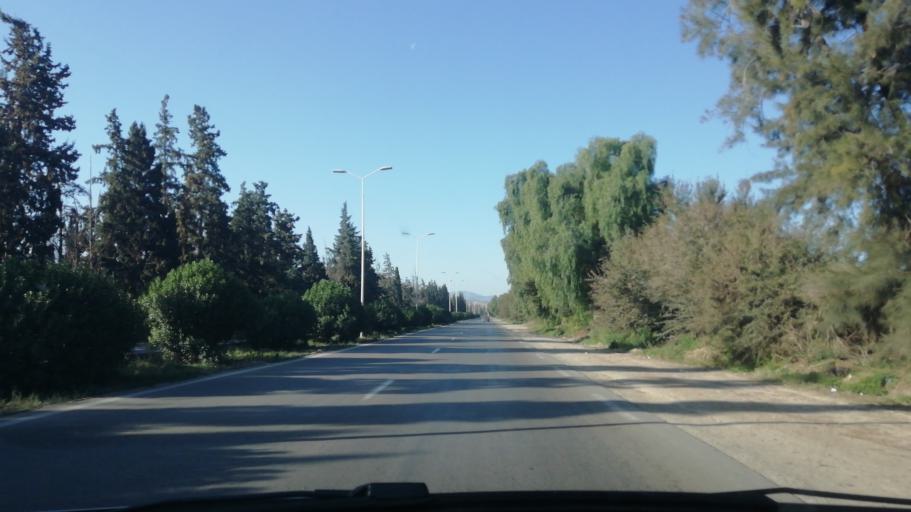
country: DZ
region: Mascara
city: Mascara
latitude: 35.6029
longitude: 0.0866
